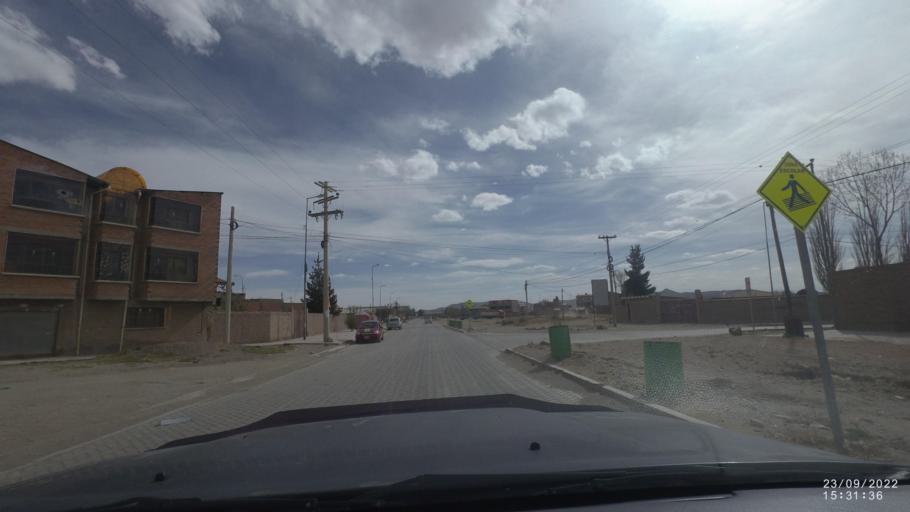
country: BO
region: Oruro
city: Oruro
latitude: -17.9741
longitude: -67.0541
